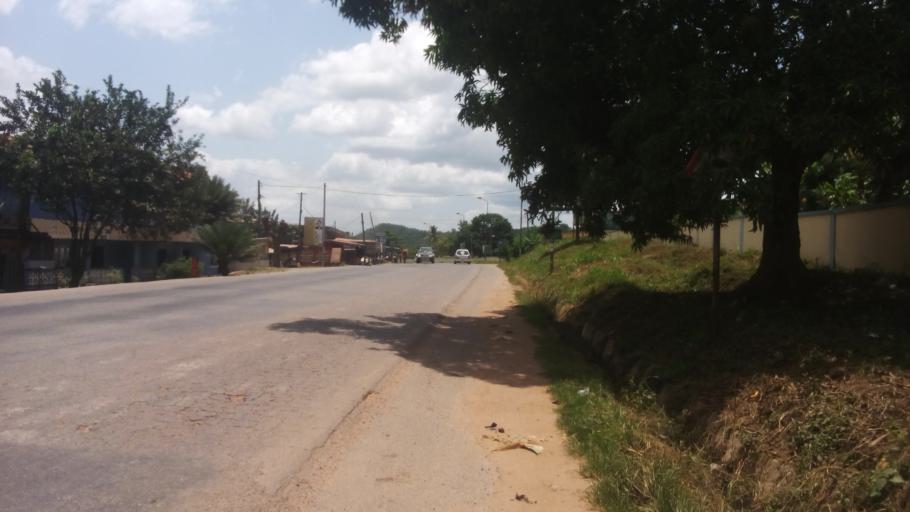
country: GH
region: Western
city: Tarkwa
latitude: 5.2941
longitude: -2.0023
